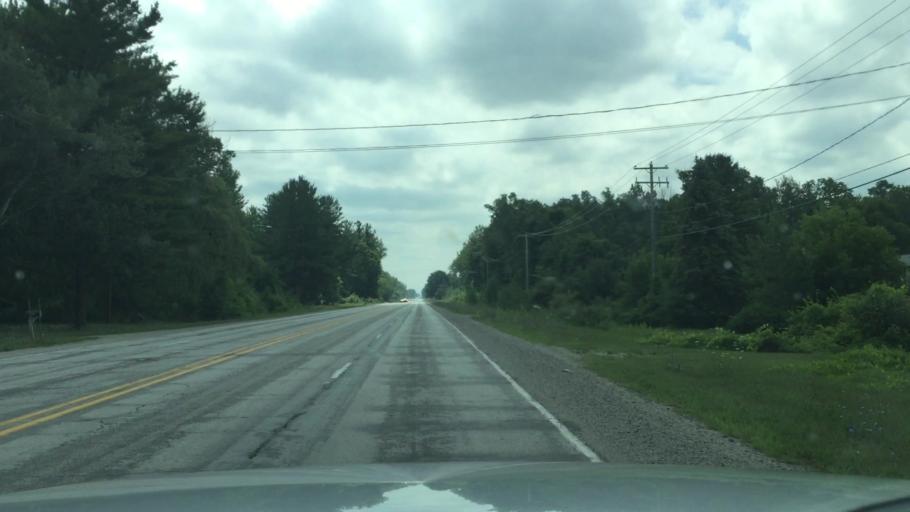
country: US
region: Michigan
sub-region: Saginaw County
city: Birch Run
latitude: 43.2881
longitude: -83.7980
